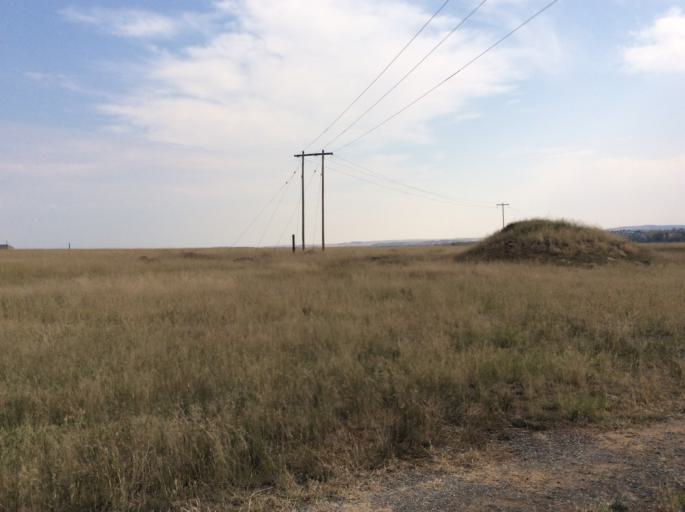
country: LS
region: Mafeteng
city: Mafeteng
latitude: -29.7336
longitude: 27.0253
